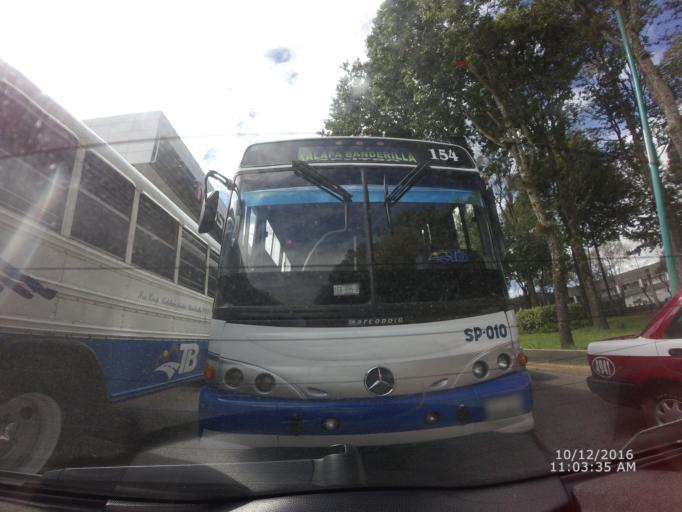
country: TR
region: Sivas
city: Karayun
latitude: 39.6722
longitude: 37.2354
